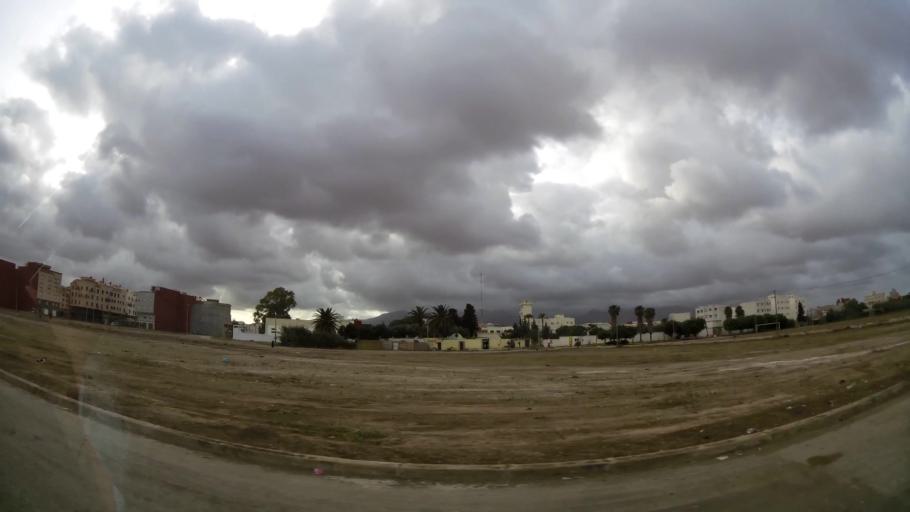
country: MA
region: Oriental
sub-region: Nador
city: Nador
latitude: 35.1558
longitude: -2.9252
